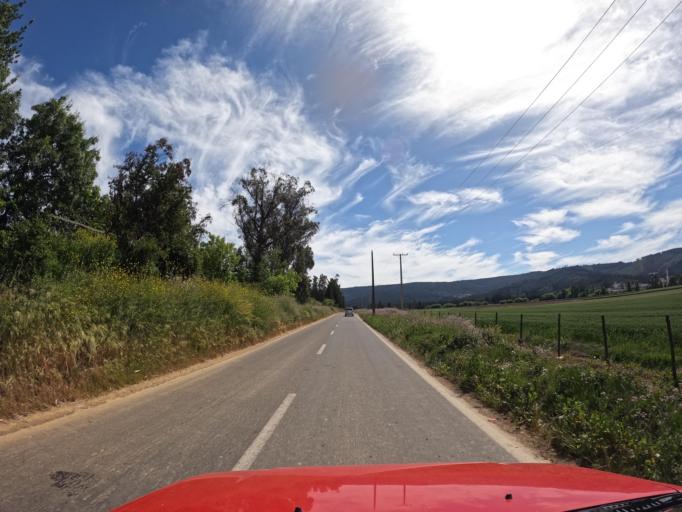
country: CL
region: Maule
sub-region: Provincia de Talca
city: Constitucion
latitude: -34.9941
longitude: -72.0135
